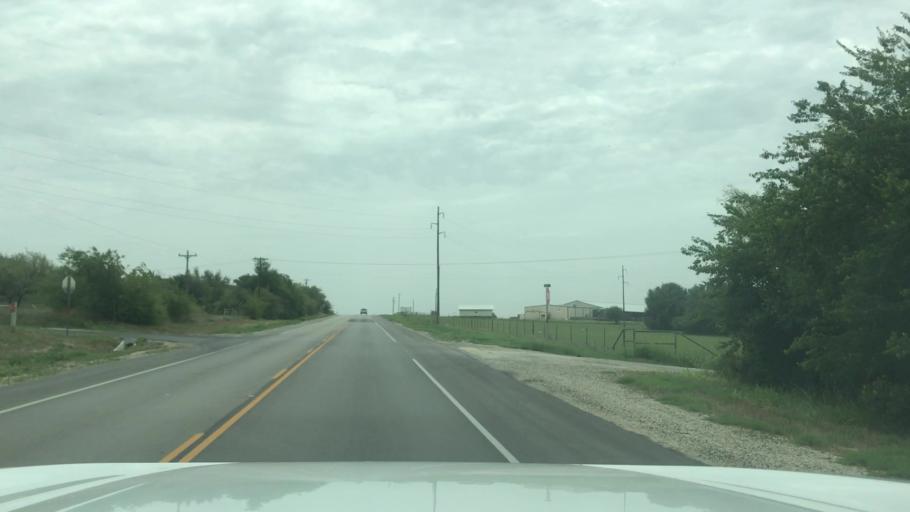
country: US
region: Texas
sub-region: Erath County
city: Dublin
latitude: 32.0879
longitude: -98.2583
